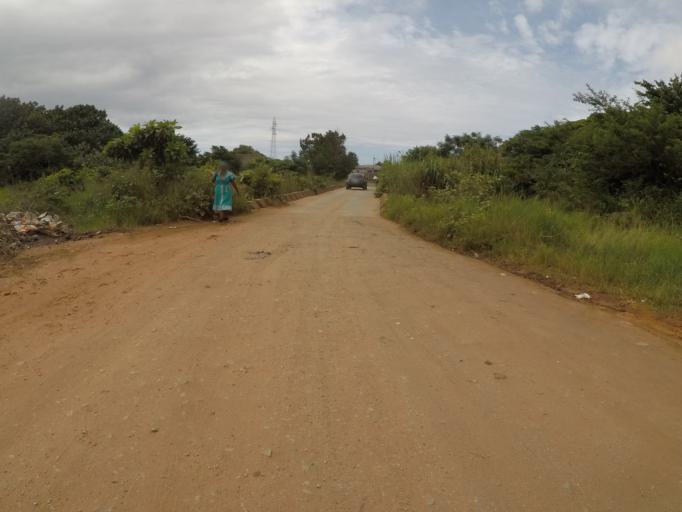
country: ZA
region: KwaZulu-Natal
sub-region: uThungulu District Municipality
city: eSikhawini
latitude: -28.8589
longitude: 31.9168
